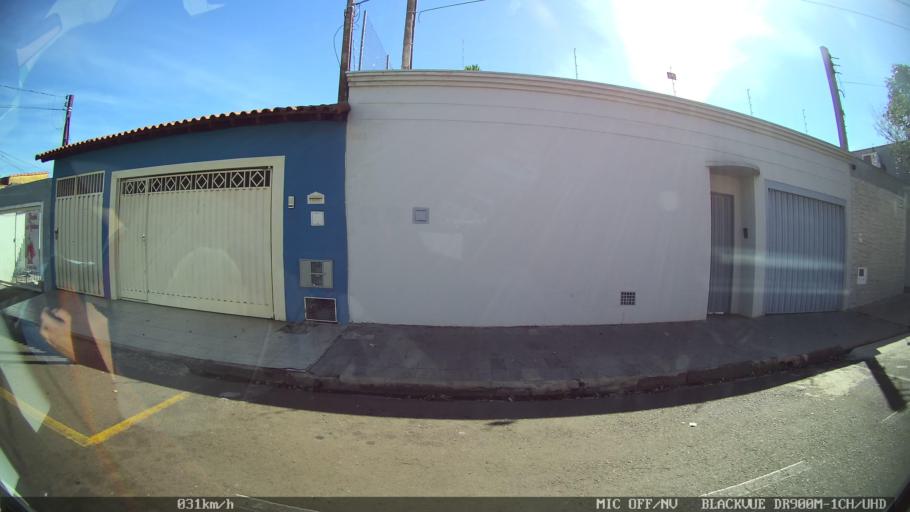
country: BR
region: Sao Paulo
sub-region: Franca
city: Franca
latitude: -20.5460
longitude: -47.3912
